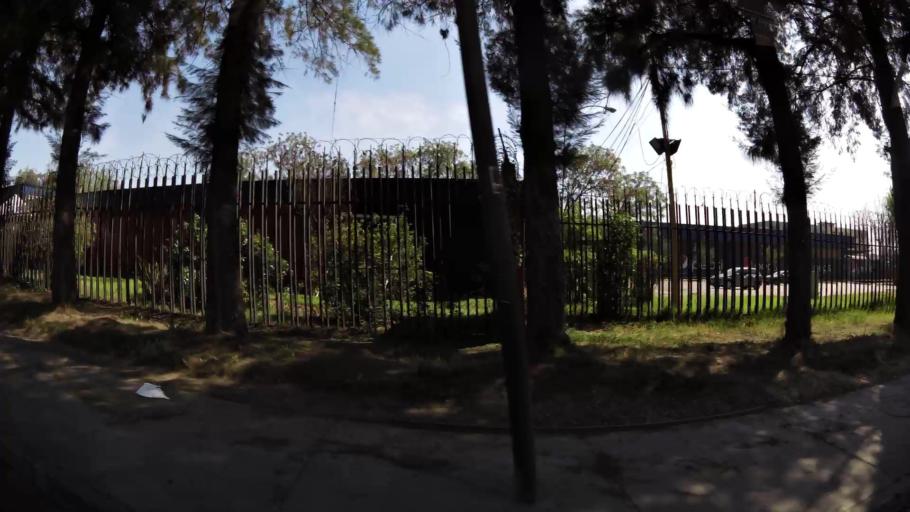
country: CL
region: Santiago Metropolitan
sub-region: Provincia de Santiago
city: Santiago
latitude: -33.4104
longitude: -70.6800
